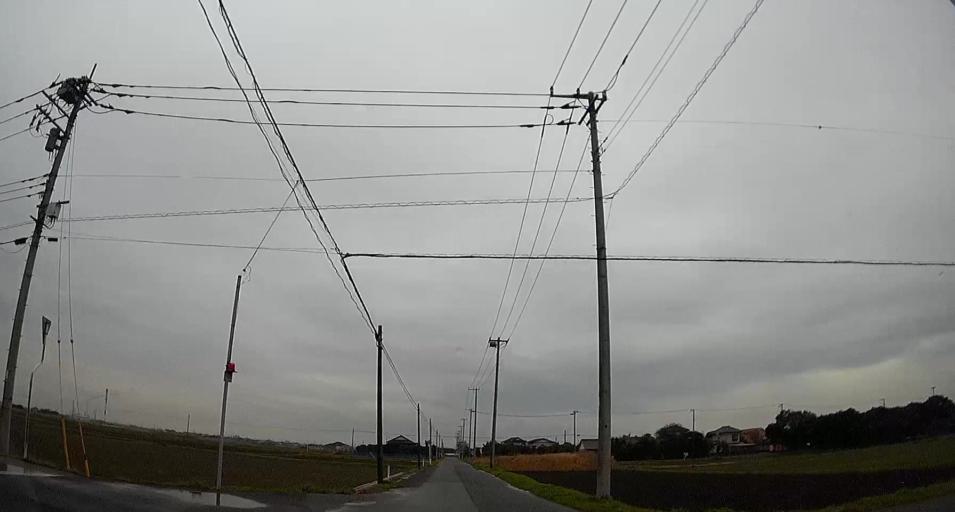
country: JP
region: Chiba
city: Kisarazu
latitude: 35.4225
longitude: 139.9055
